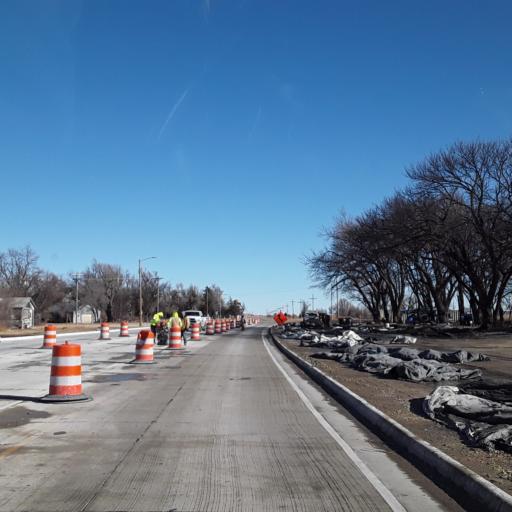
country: US
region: Kansas
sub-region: Pawnee County
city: Larned
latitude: 38.0759
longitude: -99.2426
